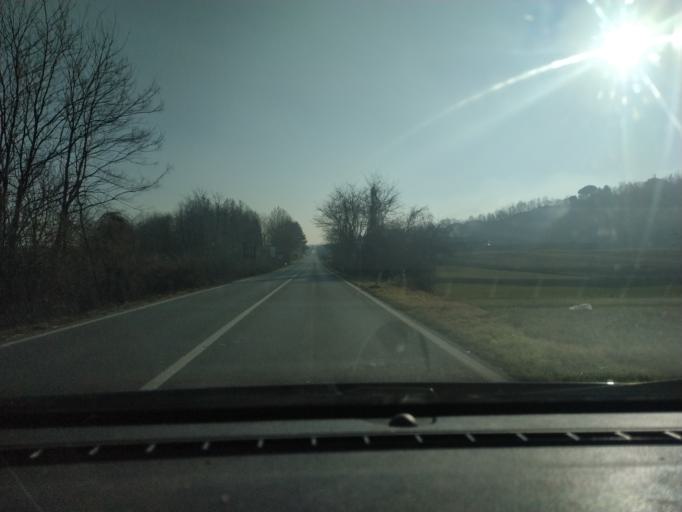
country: IT
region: Piedmont
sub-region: Provincia di Torino
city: Strambino
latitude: 45.3917
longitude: 7.8846
